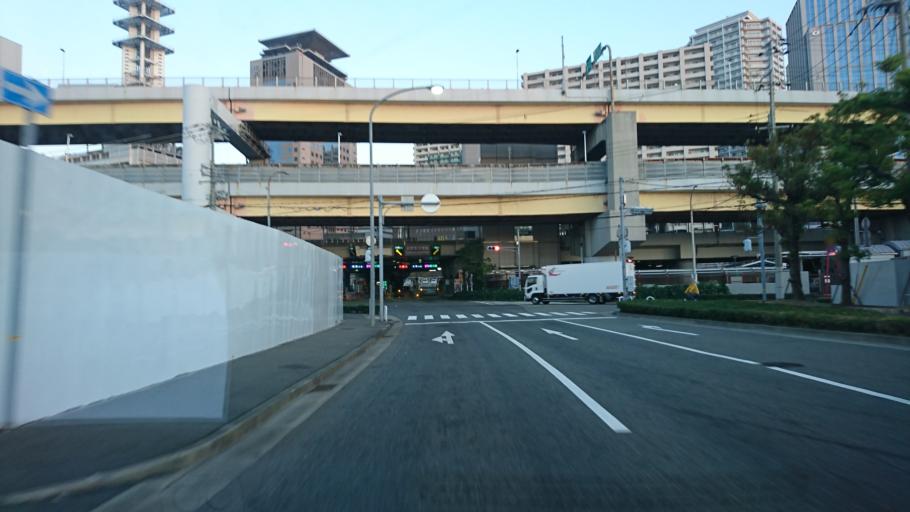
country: JP
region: Hyogo
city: Kobe
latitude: 34.6844
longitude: 135.1956
